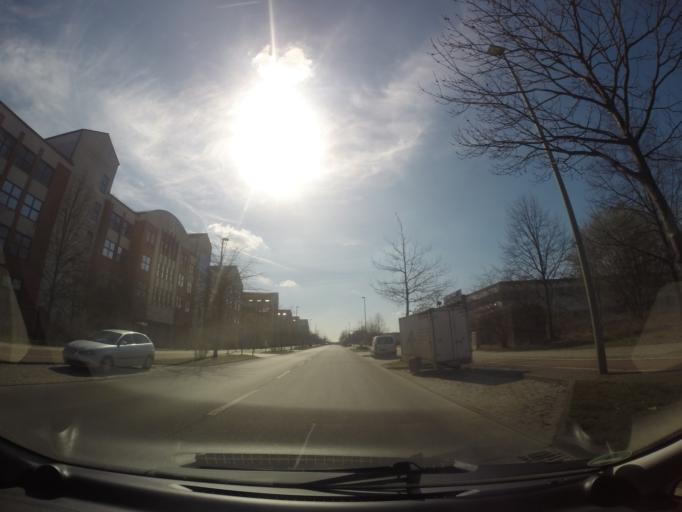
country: DE
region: Berlin
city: Falkenberg
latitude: 52.5621
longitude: 13.5525
